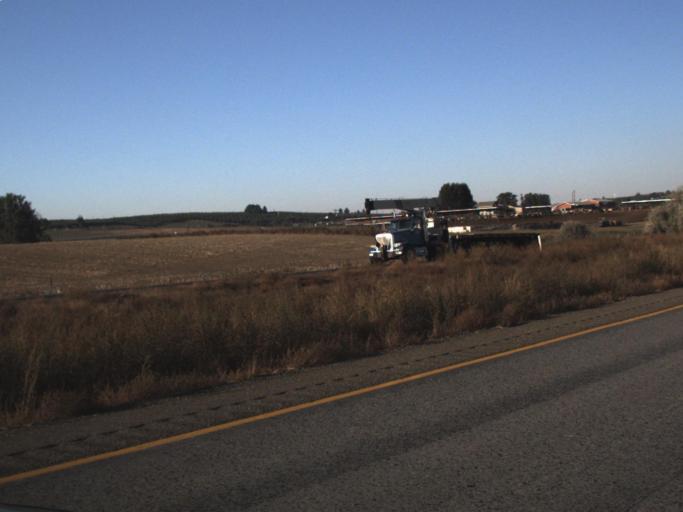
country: US
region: Washington
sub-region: Yakima County
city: Granger
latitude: 46.3386
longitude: -120.1430
